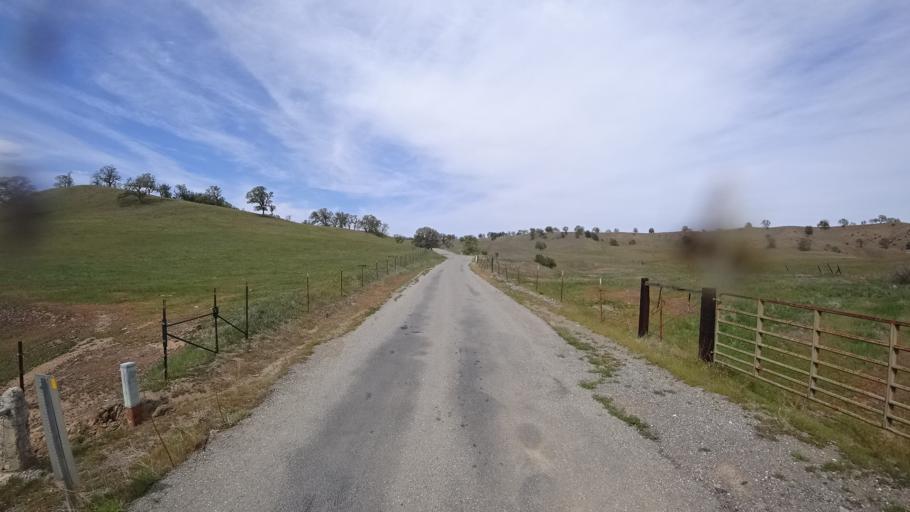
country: US
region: California
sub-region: Glenn County
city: Willows
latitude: 39.6080
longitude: -122.5594
